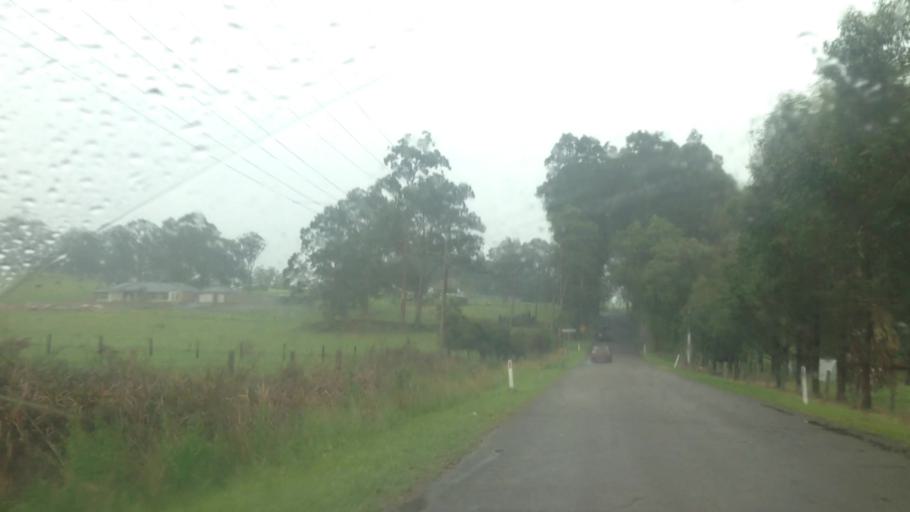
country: AU
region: New South Wales
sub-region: Wyong Shire
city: Little Jilliby
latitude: -33.2036
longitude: 151.3637
